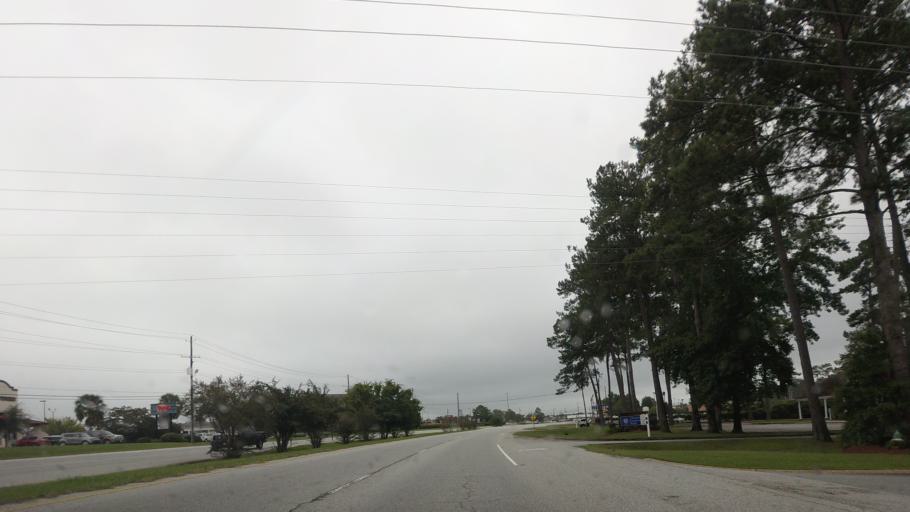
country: US
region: Georgia
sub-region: Lowndes County
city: Remerton
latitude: 30.8779
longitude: -83.2945
